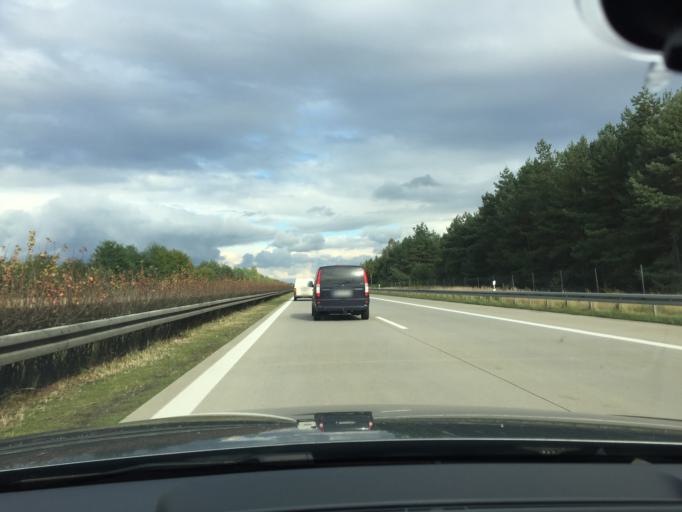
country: DE
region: Brandenburg
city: Kroppen
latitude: 51.4297
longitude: 13.8210
